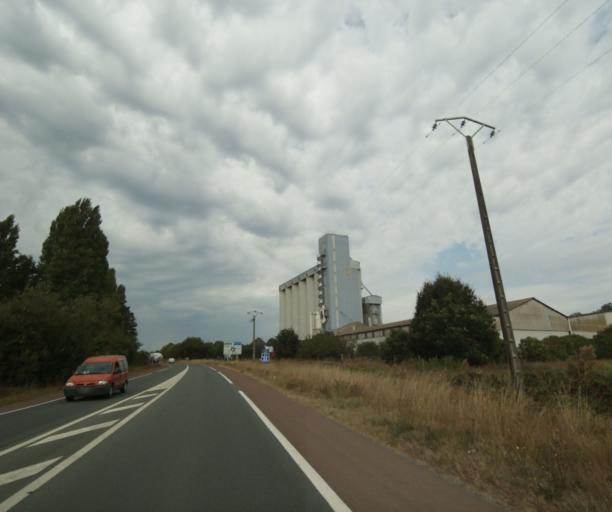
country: FR
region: Poitou-Charentes
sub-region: Departement de la Charente-Maritime
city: Tonnay-Charente
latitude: 45.9527
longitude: -0.8740
